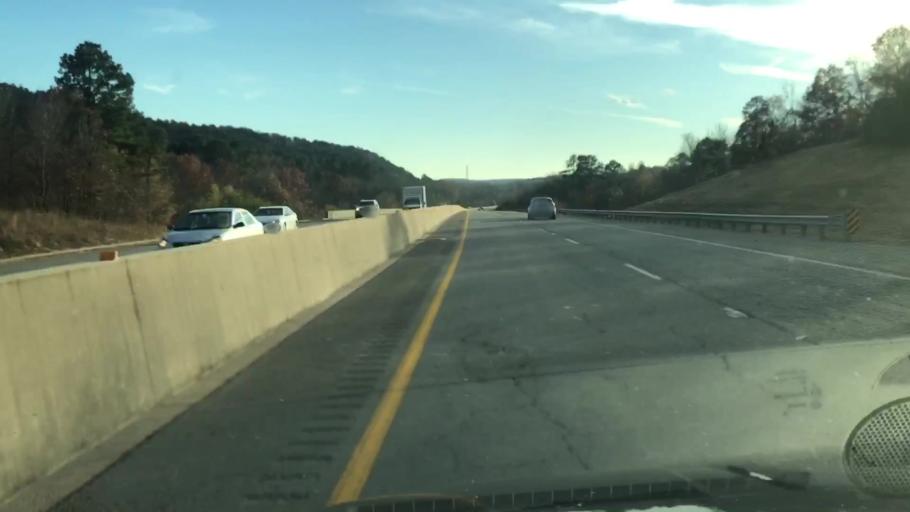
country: US
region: Arkansas
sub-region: Garland County
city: Hot Springs
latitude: 34.4870
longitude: -92.9806
